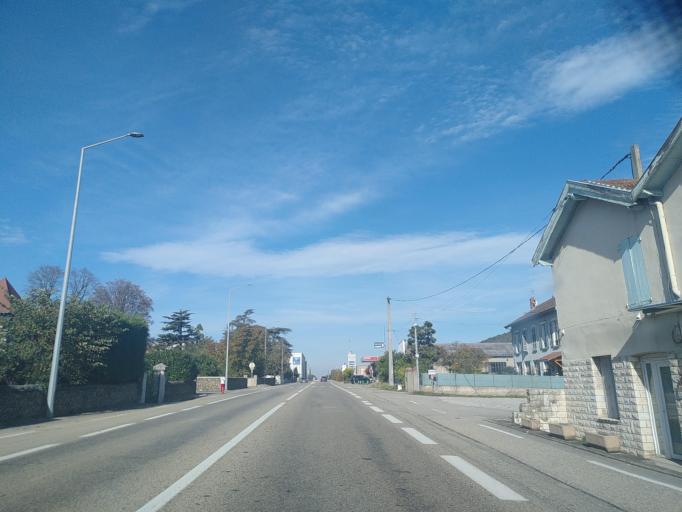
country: FR
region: Rhone-Alpes
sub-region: Departement de la Drome
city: Saint-Vallier
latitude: 45.1901
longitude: 4.8142
